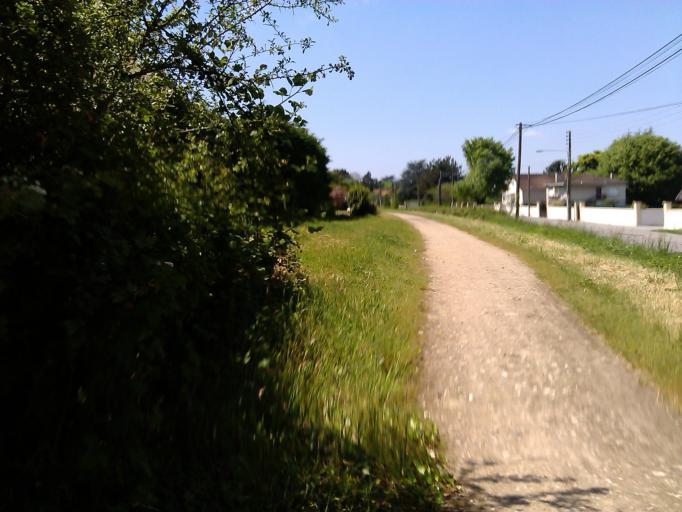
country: FR
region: Centre
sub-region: Departement de l'Indre
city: Saint-Gaultier
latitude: 46.6341
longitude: 1.4364
